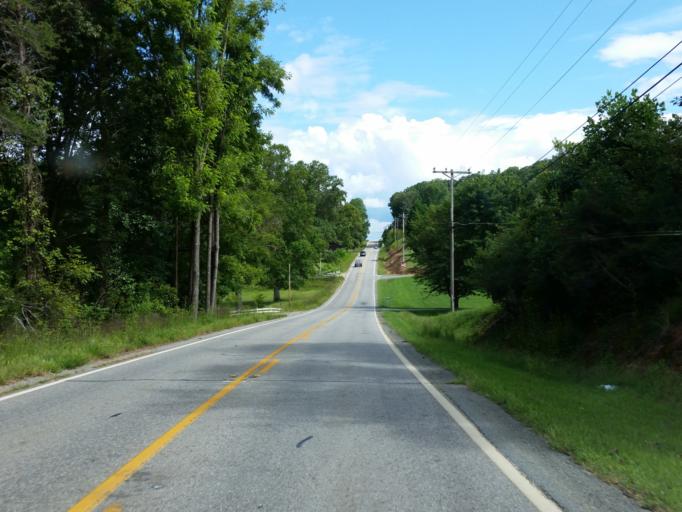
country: US
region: Georgia
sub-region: Fannin County
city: Blue Ridge
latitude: 34.8840
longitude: -84.2545
